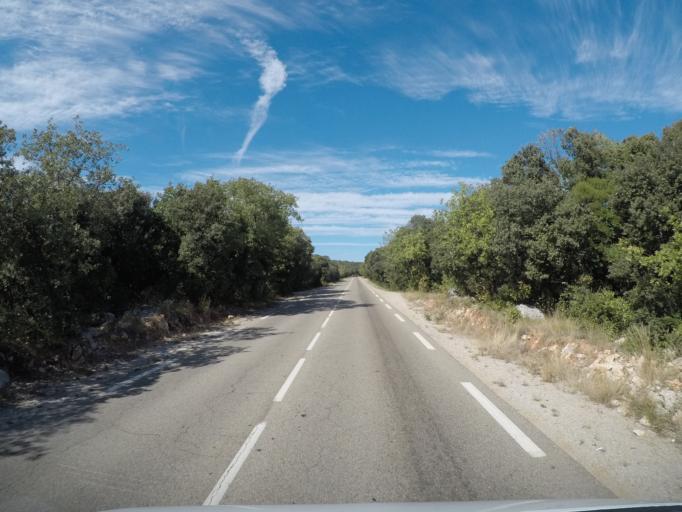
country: FR
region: Languedoc-Roussillon
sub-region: Departement de l'Herault
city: Saint-Martin-de-Londres
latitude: 43.7631
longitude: 3.7471
